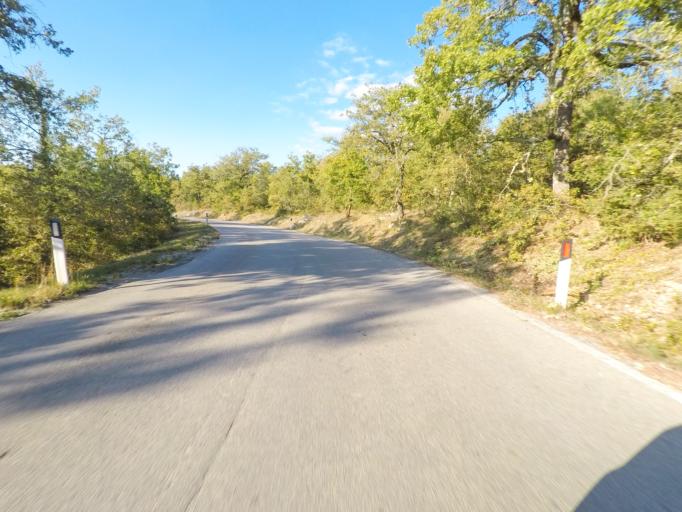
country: IT
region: Tuscany
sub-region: Provincia di Siena
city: Radda in Chianti
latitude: 43.4532
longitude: 11.3862
